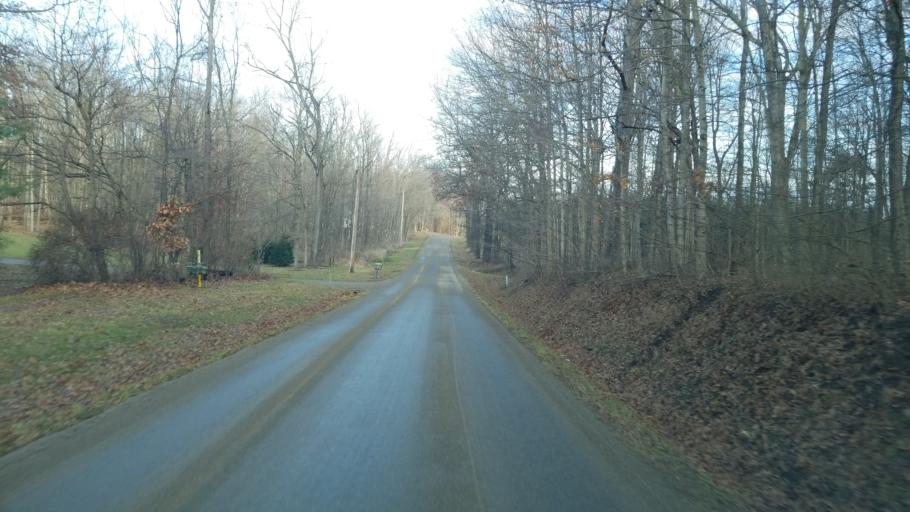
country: US
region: Ohio
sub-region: Knox County
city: Gambier
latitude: 40.3300
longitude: -82.3822
